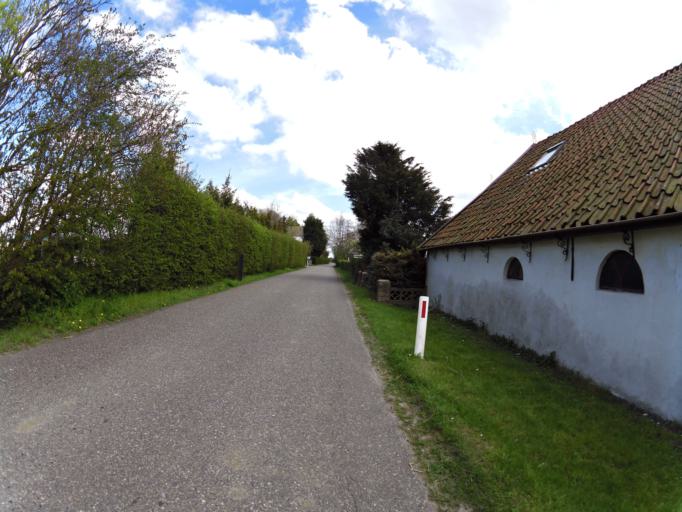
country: NL
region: South Holland
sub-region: Gemeente Hellevoetsluis
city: Nieuwenhoorn
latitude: 51.8869
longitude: 4.1228
